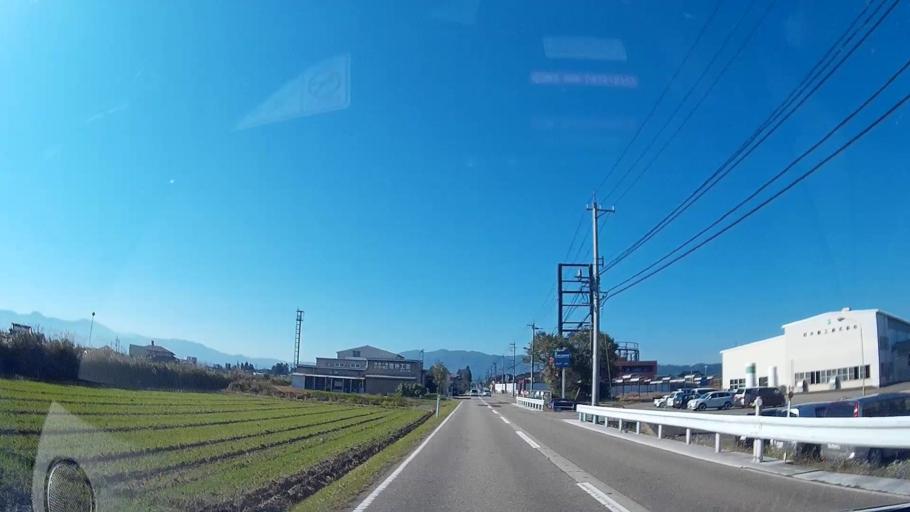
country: JP
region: Toyama
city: Nanto-shi
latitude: 36.5780
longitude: 136.9013
